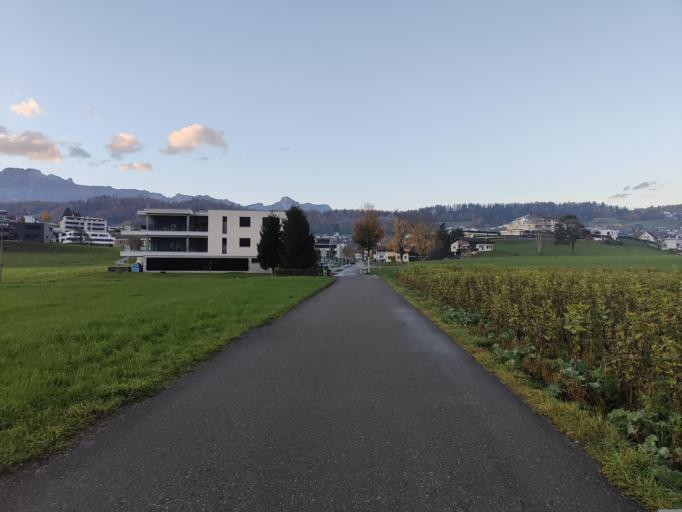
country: LI
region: Mauren
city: Mauren
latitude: 47.2120
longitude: 9.5429
